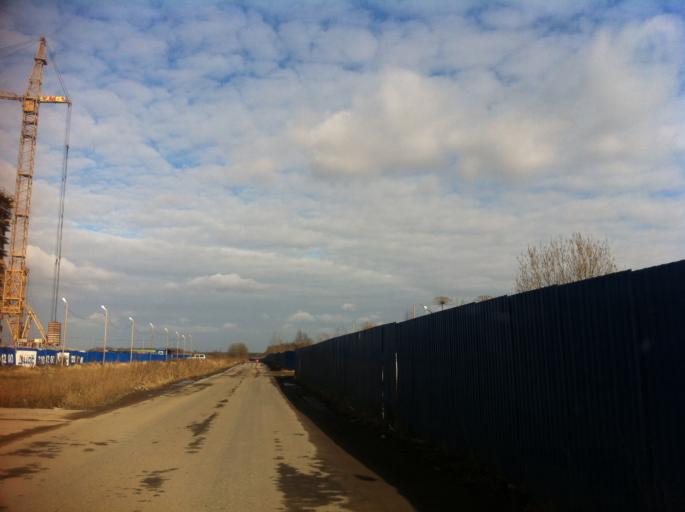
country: RU
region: Leningrad
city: Yanino Vtoroye
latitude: 59.9493
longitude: 30.5758
